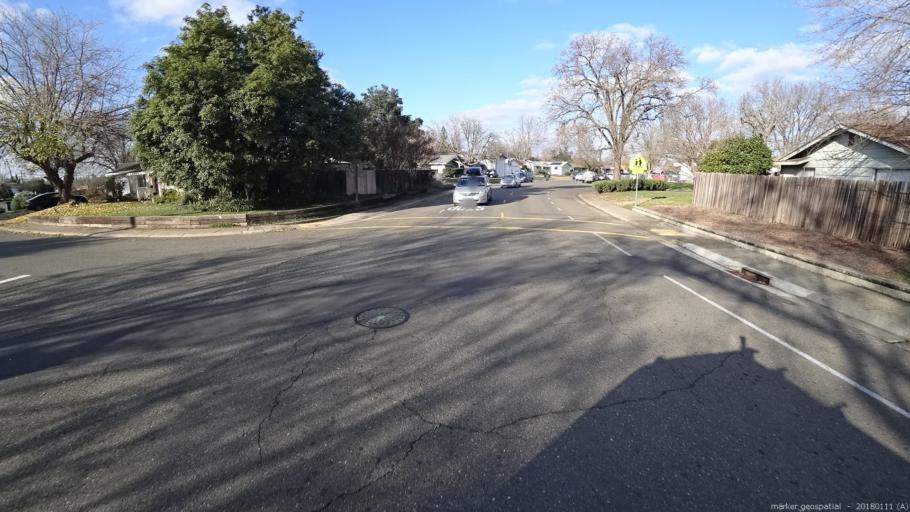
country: US
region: California
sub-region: Sacramento County
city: Rancho Cordova
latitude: 38.6055
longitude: -121.3024
